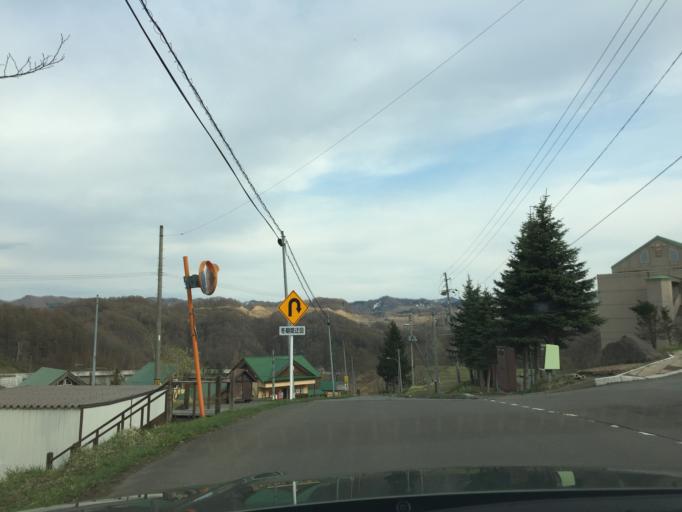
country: JP
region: Hokkaido
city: Utashinai
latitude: 43.5219
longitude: 142.0198
